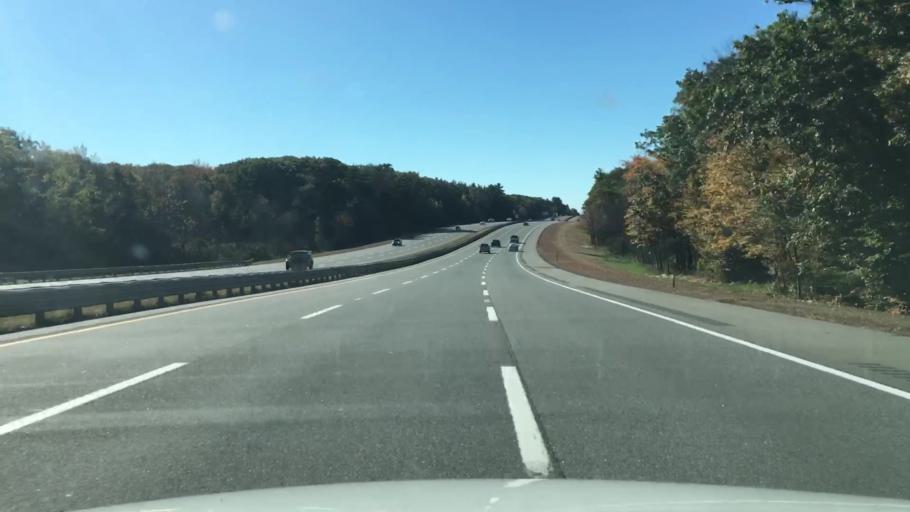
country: US
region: Maine
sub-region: York County
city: Cape Neddick
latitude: 43.1897
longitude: -70.6458
